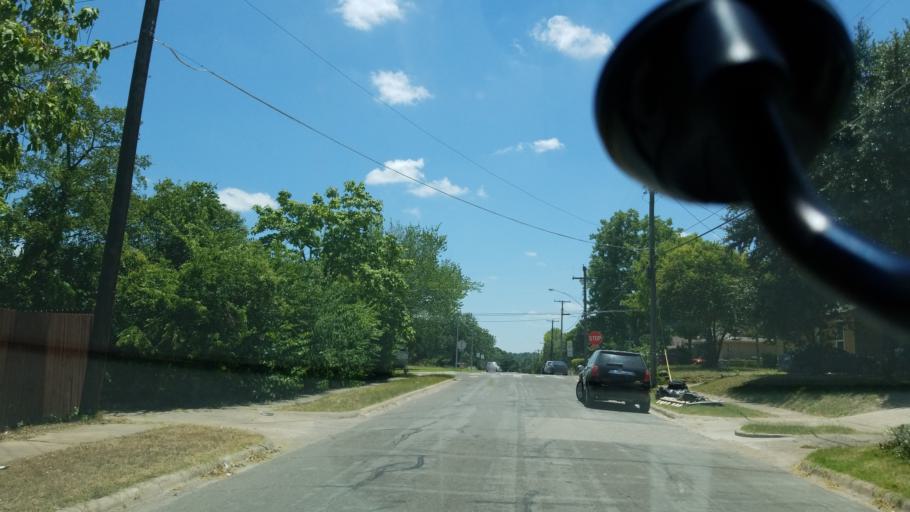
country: US
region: Texas
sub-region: Dallas County
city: Cockrell Hill
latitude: 32.6966
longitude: -96.8118
